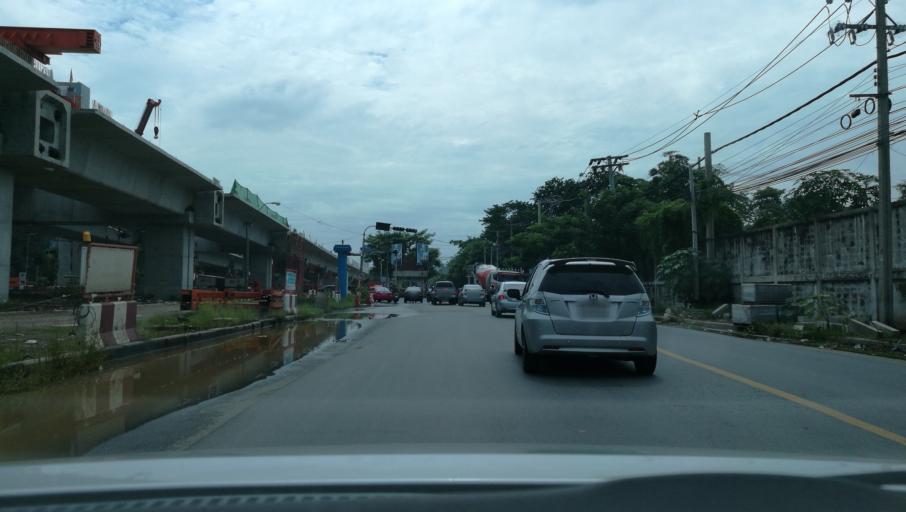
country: TH
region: Bangkok
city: Phaya Thai
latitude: 13.7933
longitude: 100.5352
